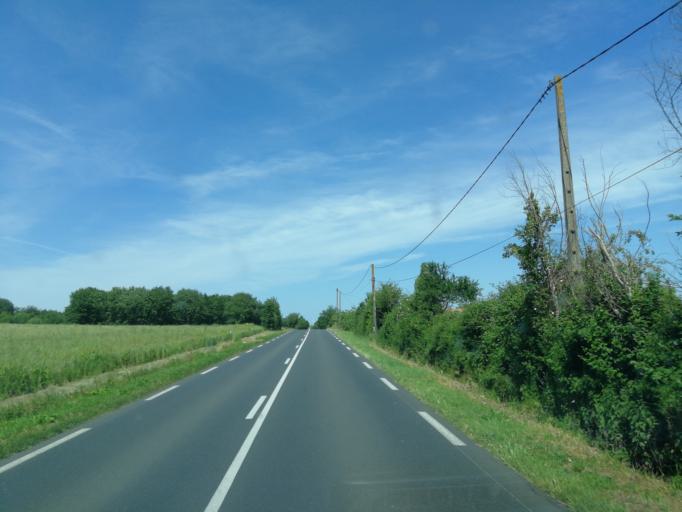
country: FR
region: Poitou-Charentes
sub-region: Departement des Deux-Sevres
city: Saint-Jean-de-Thouars
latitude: 46.9403
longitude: -0.2393
